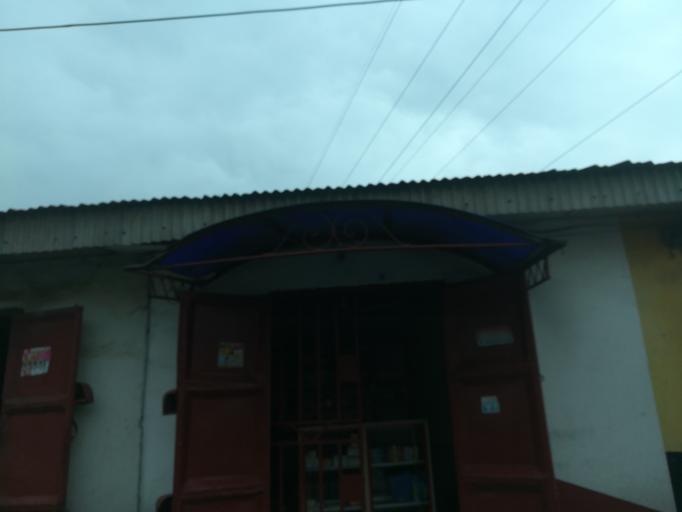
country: NG
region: Rivers
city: Port Harcourt
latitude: 4.8158
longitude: 7.0198
